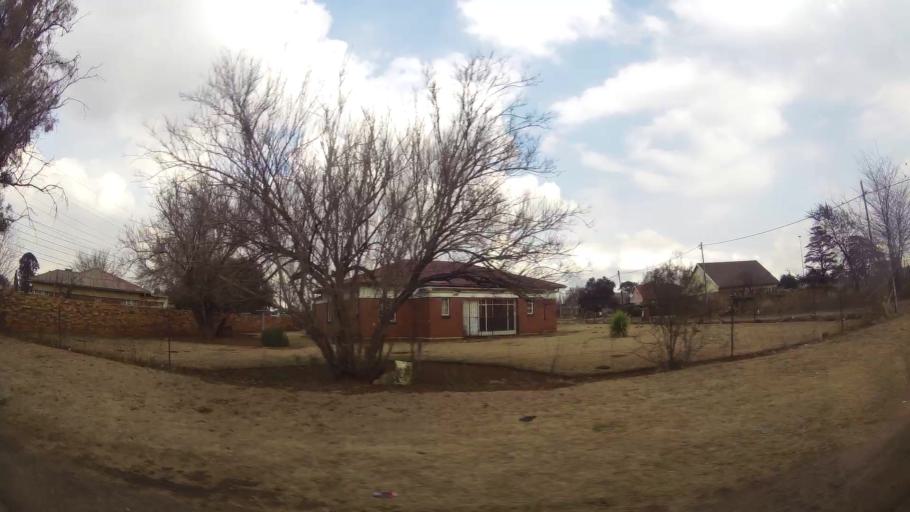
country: ZA
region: Gauteng
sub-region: Sedibeng District Municipality
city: Vereeniging
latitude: -26.6724
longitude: 27.9376
